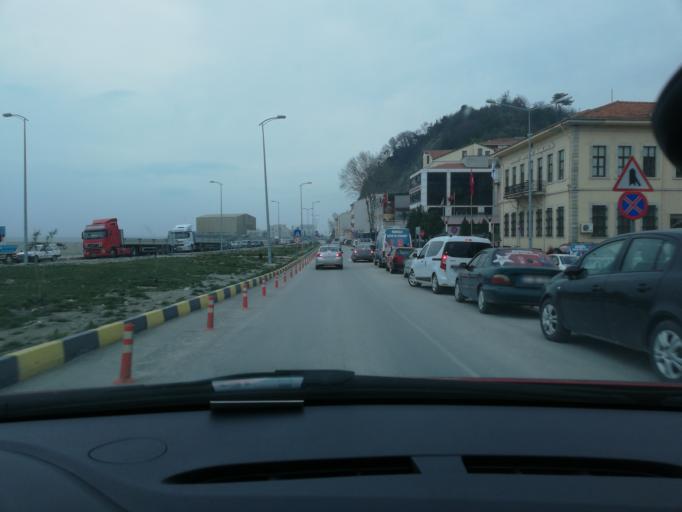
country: TR
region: Kastamonu
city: Inebolu
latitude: 41.9792
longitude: 33.7597
